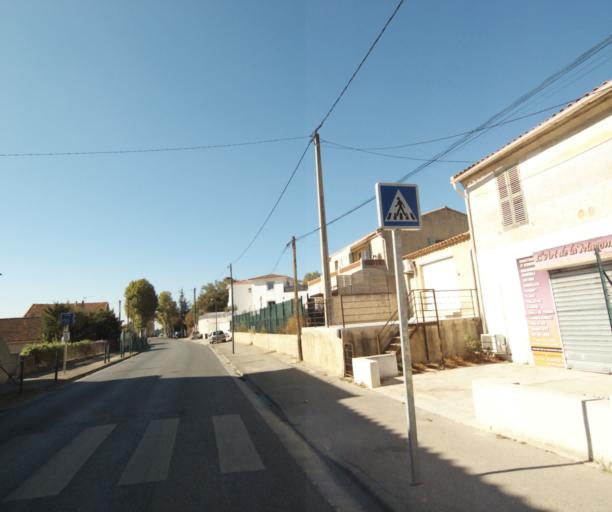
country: FR
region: Provence-Alpes-Cote d'Azur
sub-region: Departement des Bouches-du-Rhone
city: Plan-de-Cuques
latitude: 43.3511
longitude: 5.4718
